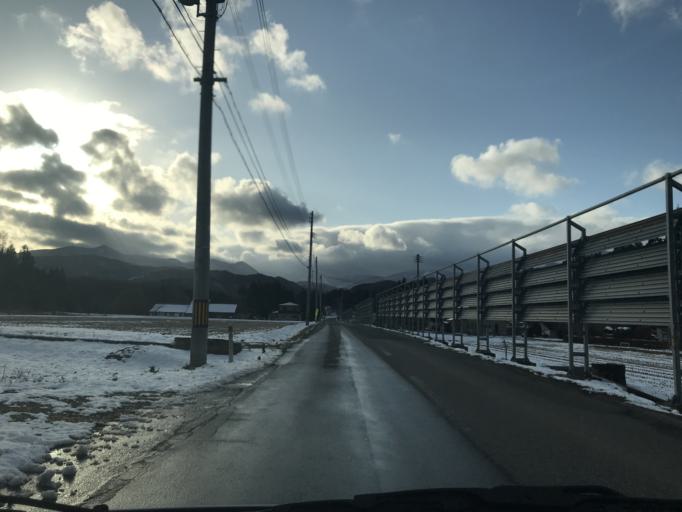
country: JP
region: Iwate
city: Kitakami
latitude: 39.2438
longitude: 140.9941
